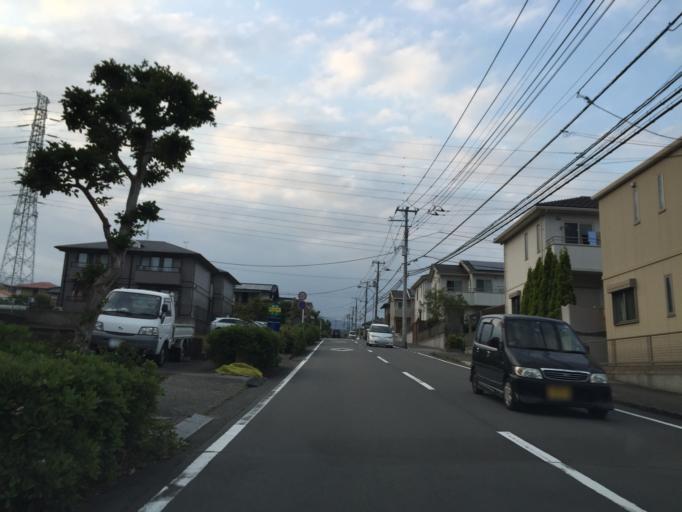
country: JP
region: Shizuoka
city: Numazu
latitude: 35.1317
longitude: 138.8589
